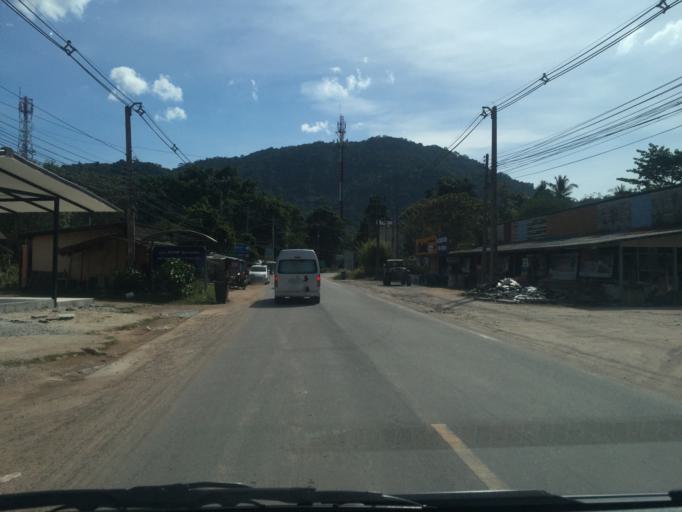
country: TH
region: Trat
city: Laem Ngop
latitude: 12.1348
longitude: 102.2760
